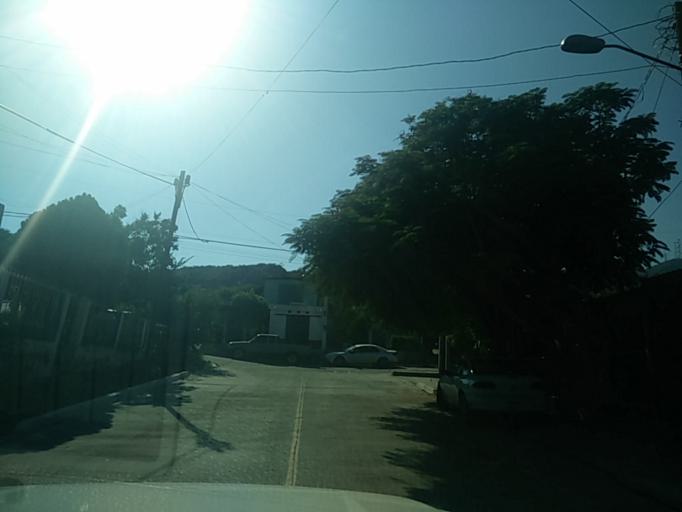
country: MX
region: Sonora
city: Heroica Guaymas
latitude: 27.9368
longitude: -110.8835
